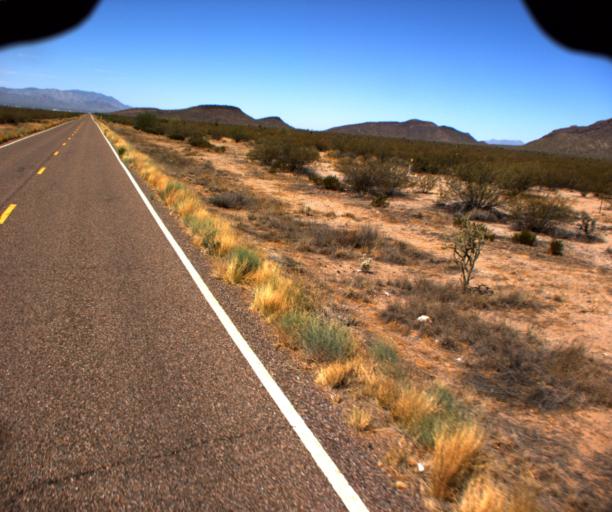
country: US
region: Arizona
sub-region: Yavapai County
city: Congress
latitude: 34.0300
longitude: -113.0841
